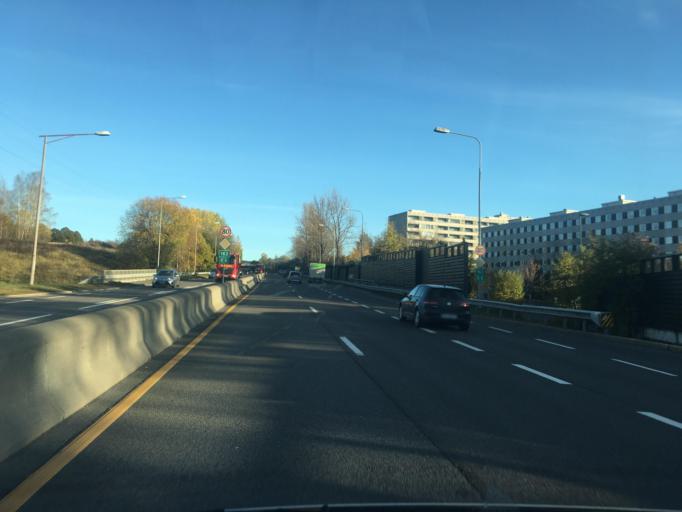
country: NO
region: Akershus
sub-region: Lorenskog
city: Kjenn
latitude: 59.9531
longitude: 10.9134
